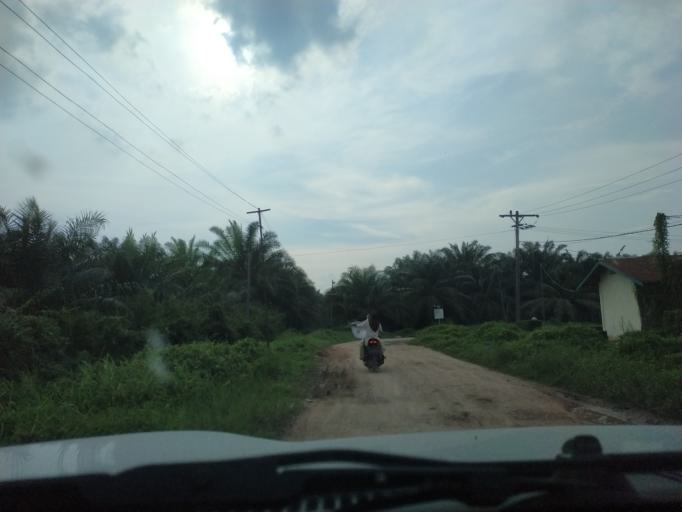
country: ID
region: North Sumatra
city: Rantauprapat
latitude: 2.3054
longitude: 100.0705
